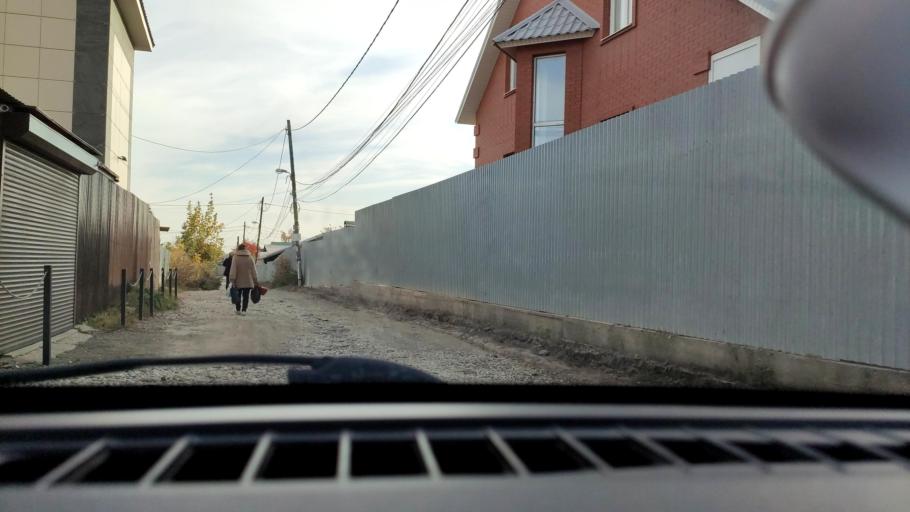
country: RU
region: Samara
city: Petra-Dubrava
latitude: 53.2931
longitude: 50.2786
